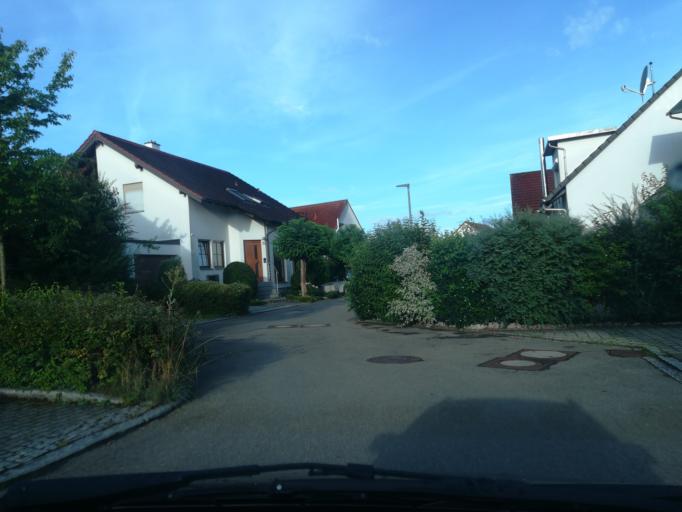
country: DE
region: Baden-Wuerttemberg
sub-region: Tuebingen Region
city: Wannweil
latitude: 48.5052
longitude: 9.1736
